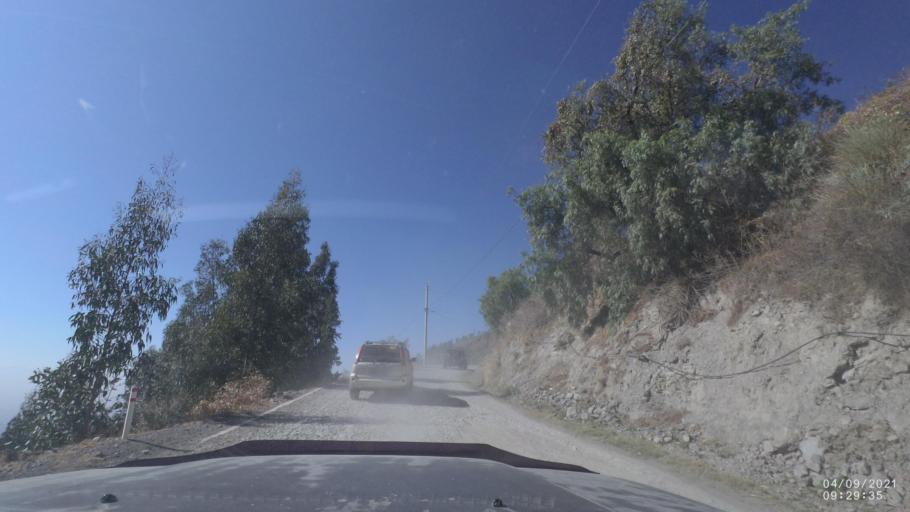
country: BO
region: Cochabamba
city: Sipe Sipe
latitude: -17.3535
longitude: -66.3750
